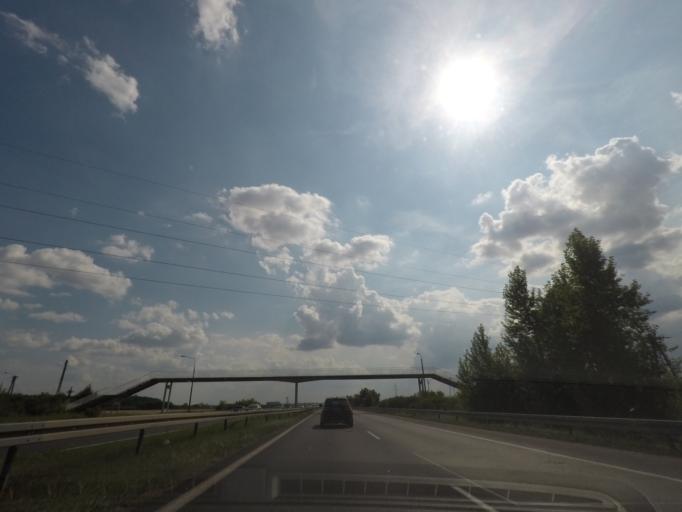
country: PL
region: Lodz Voivodeship
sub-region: Powiat piotrkowski
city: Wola Krzysztoporska
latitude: 51.3414
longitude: 19.5965
